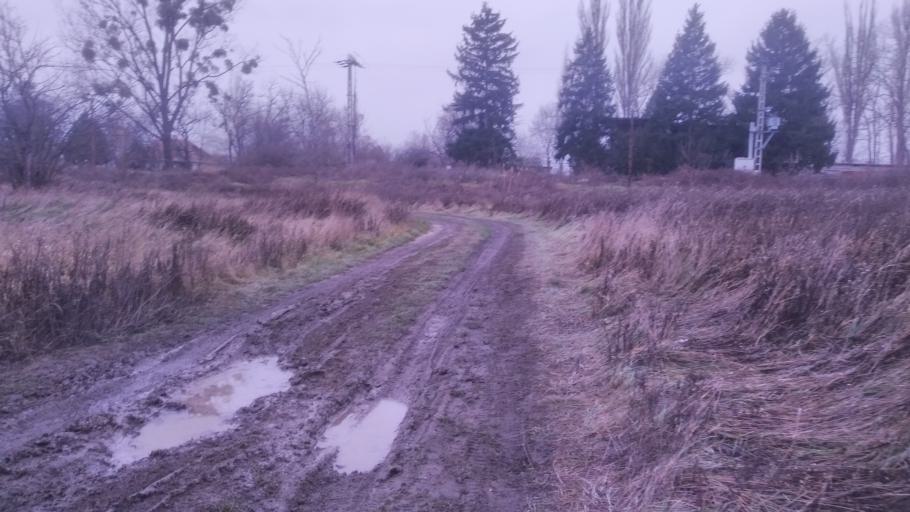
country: HU
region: Komarom-Esztergom
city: Dunaalmas
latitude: 47.7305
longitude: 18.3180
